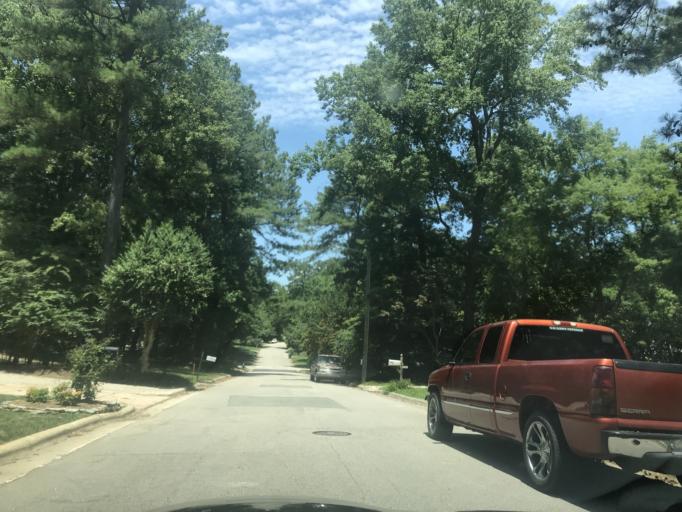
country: US
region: North Carolina
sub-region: Wake County
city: West Raleigh
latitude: 35.8911
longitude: -78.6230
